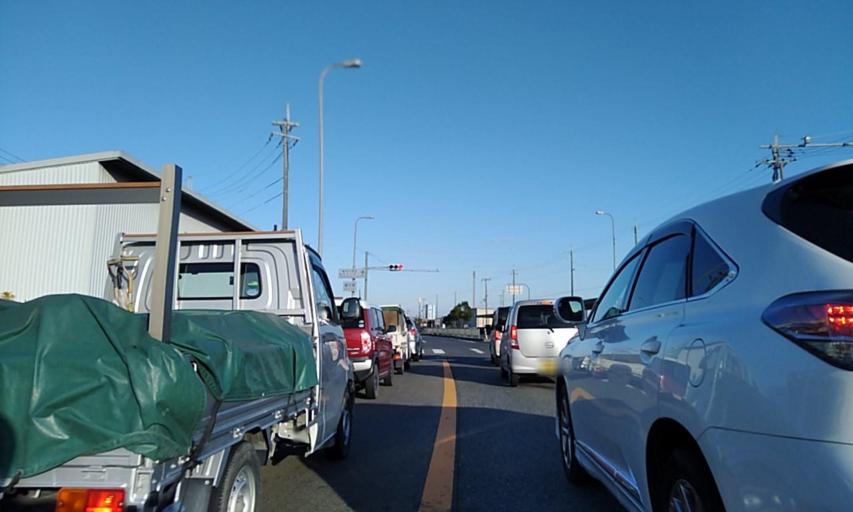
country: JP
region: Wakayama
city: Iwade
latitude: 34.3551
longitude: 135.2671
